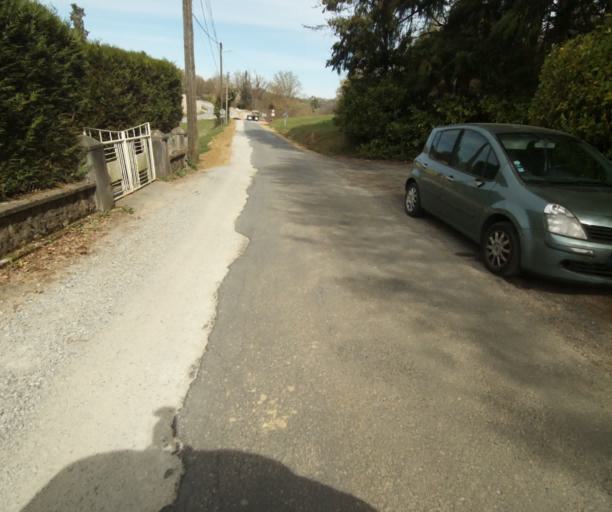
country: FR
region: Limousin
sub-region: Departement de la Correze
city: Naves
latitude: 45.3038
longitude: 1.7799
